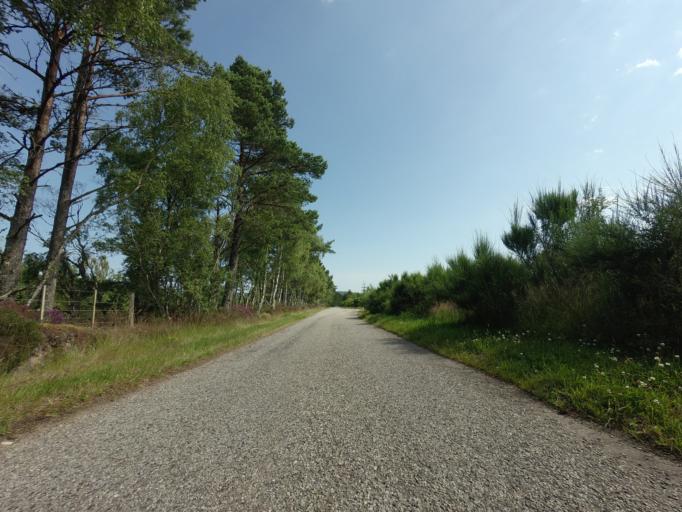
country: GB
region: Scotland
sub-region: Highland
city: Invergordon
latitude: 57.7373
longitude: -4.1870
